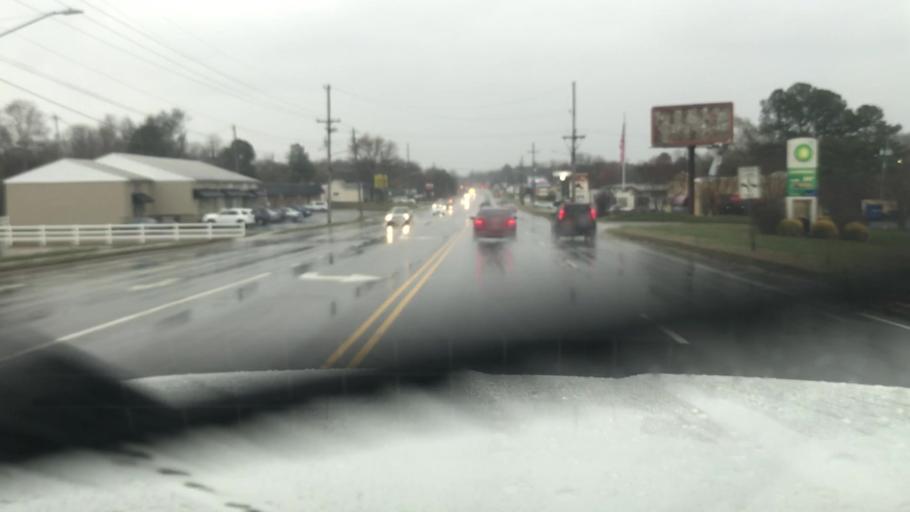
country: US
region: North Carolina
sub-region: Franklin County
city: Louisburg
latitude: 36.0903
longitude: -78.3005
